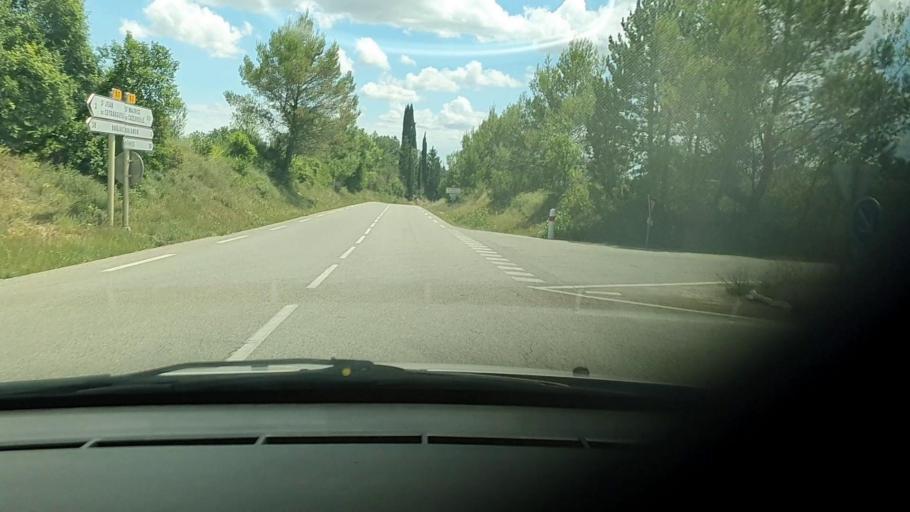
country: FR
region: Languedoc-Roussillon
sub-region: Departement du Gard
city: Moussac
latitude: 44.0365
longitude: 4.2321
